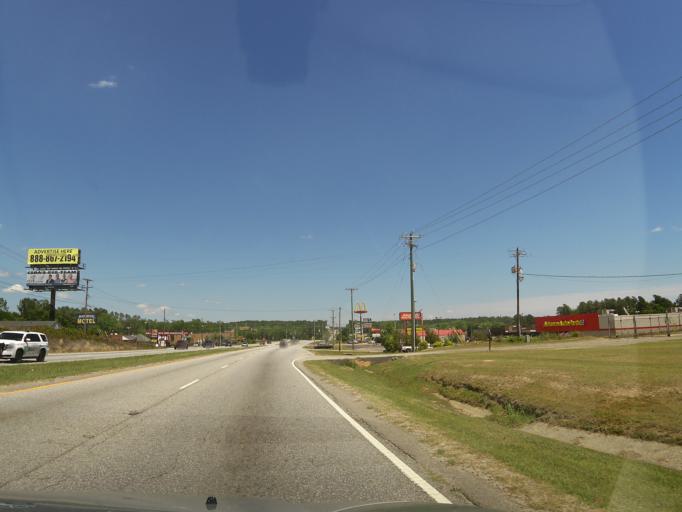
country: US
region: South Carolina
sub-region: Aiken County
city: Clearwater
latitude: 33.5030
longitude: -81.9031
